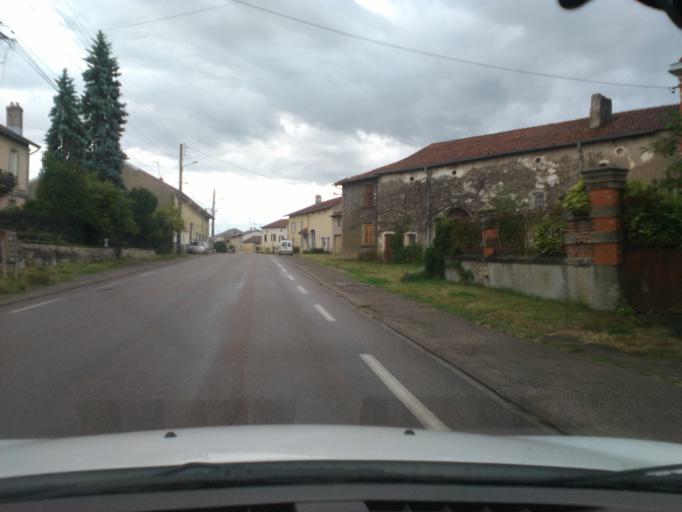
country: FR
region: Lorraine
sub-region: Departement de Meurthe-et-Moselle
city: Vezelise
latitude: 48.4216
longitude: 6.1291
